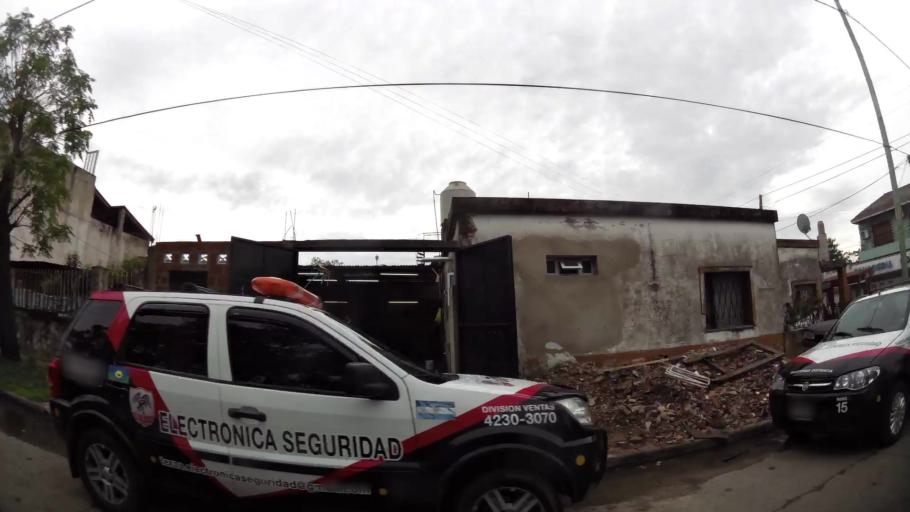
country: AR
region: Buenos Aires
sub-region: Partido de Lomas de Zamora
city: Lomas de Zamora
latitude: -34.7391
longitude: -58.3663
